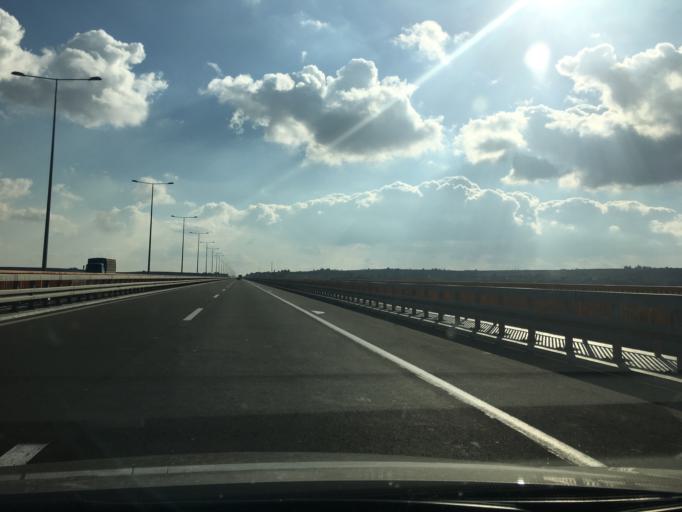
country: RS
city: Beska
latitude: 45.1793
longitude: 20.0781
